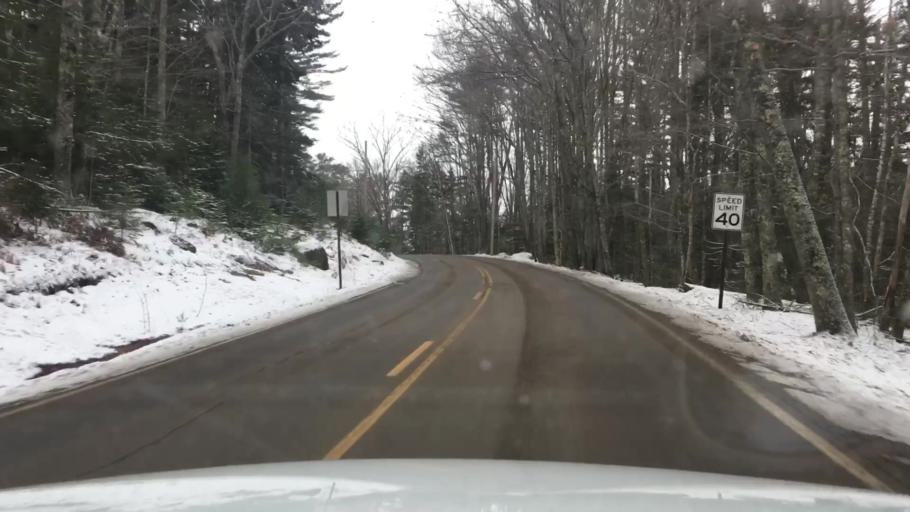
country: US
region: Maine
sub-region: Waldo County
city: Lincolnville
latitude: 44.2864
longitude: -69.0166
